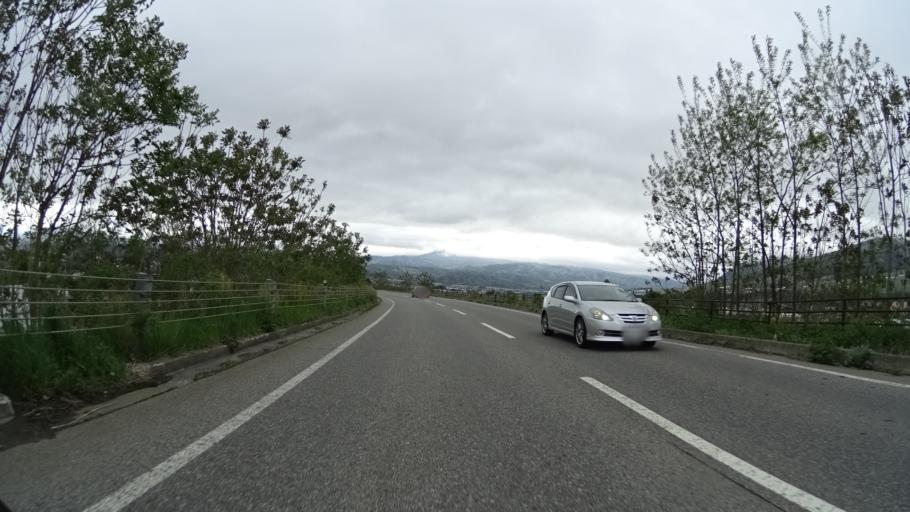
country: JP
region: Nagano
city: Nakano
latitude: 36.7594
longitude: 138.3893
